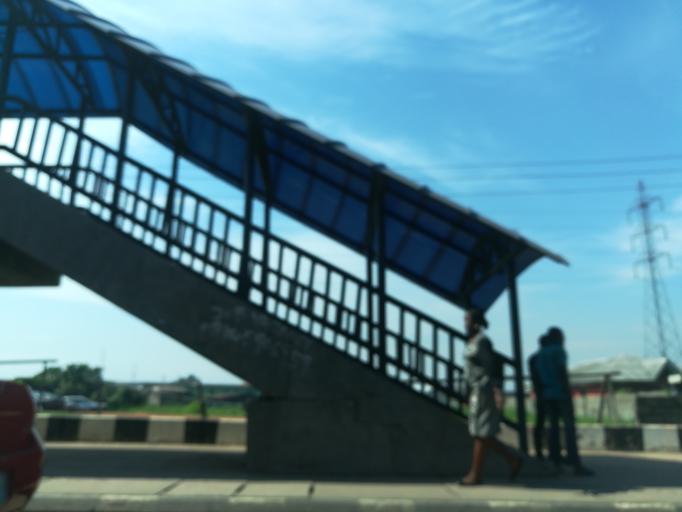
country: NG
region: Lagos
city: Ebute Ikorodu
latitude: 6.6195
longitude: 3.4726
